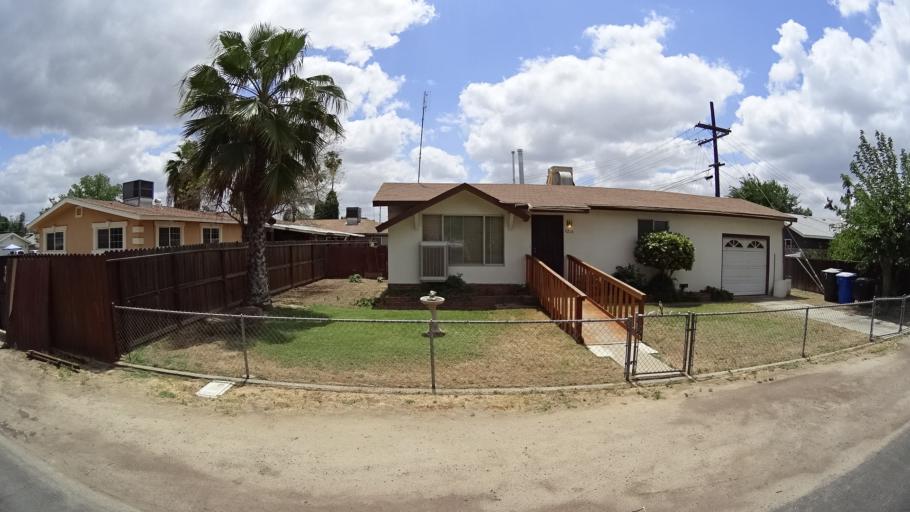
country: US
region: California
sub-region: Kings County
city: Hanford
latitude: 36.3152
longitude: -119.6632
